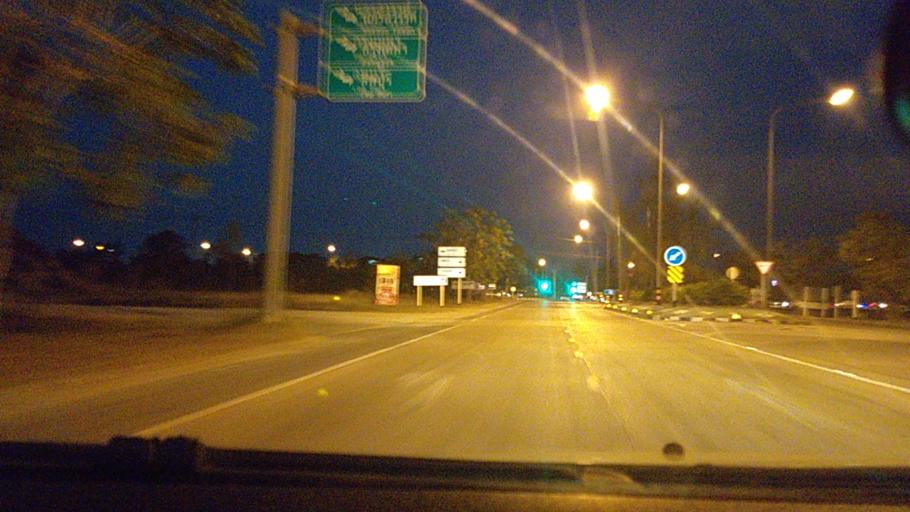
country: TH
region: Sing Buri
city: Sing Buri
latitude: 14.8757
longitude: 100.4301
